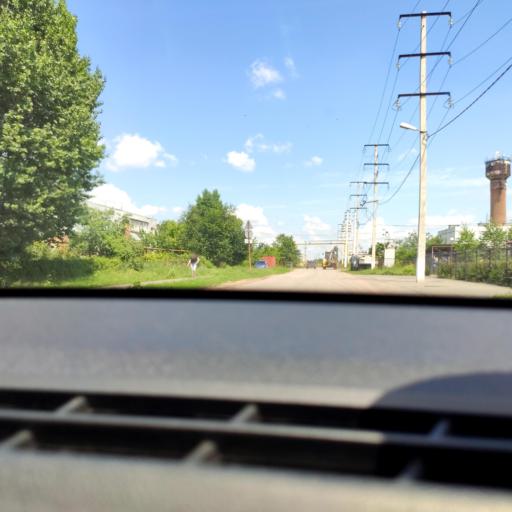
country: RU
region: Samara
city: Podstepki
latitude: 53.5184
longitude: 49.1127
